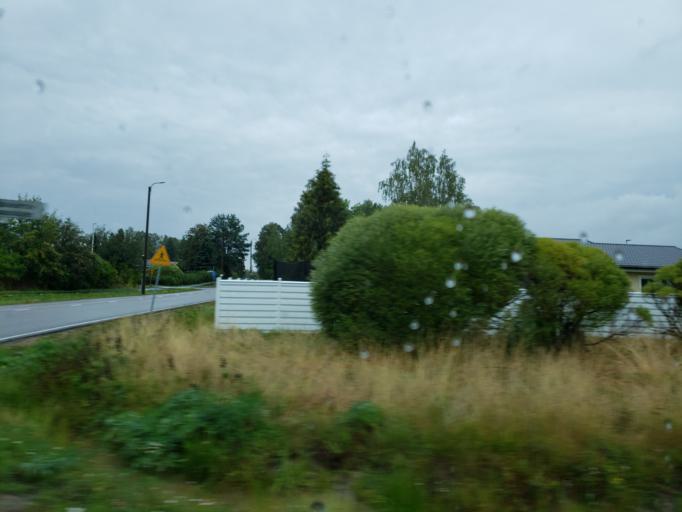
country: FI
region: Uusimaa
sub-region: Porvoo
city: Porvoo
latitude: 60.3644
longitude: 25.6251
